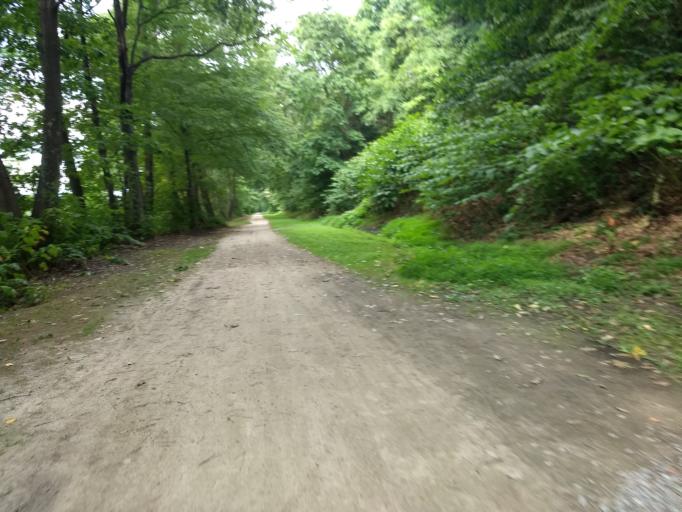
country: US
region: Pennsylvania
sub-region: Allegheny County
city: Brackenridge
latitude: 40.6202
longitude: -79.7047
